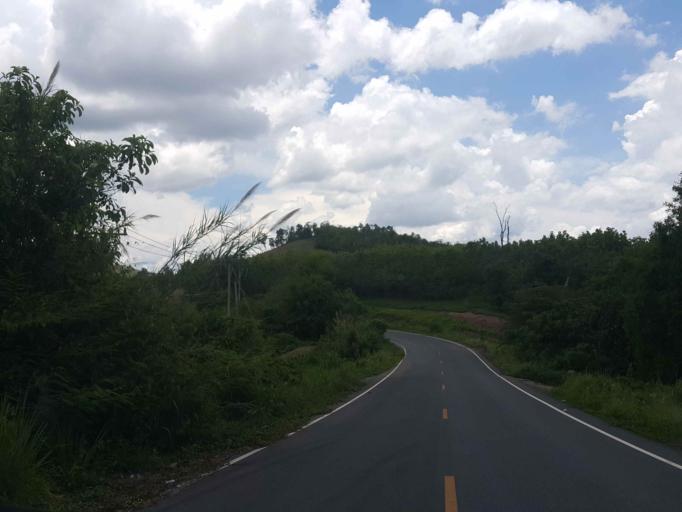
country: TH
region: Nan
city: Wiang Sa
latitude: 18.5362
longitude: 100.5490
